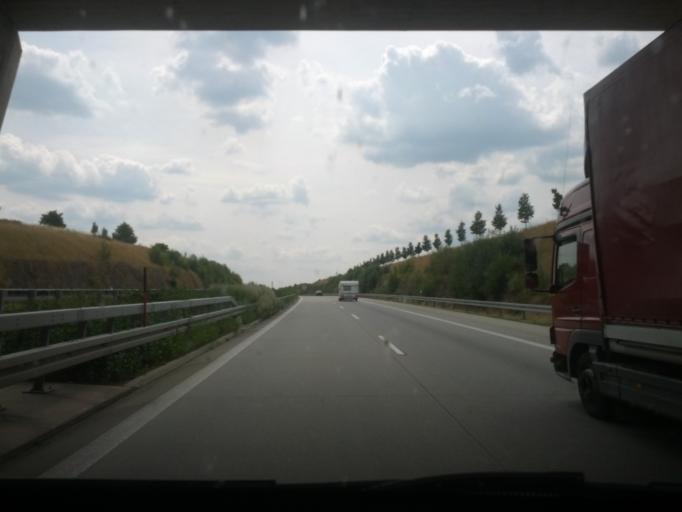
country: DE
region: Saxony
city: Liebstadt
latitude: 50.8810
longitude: 13.8743
